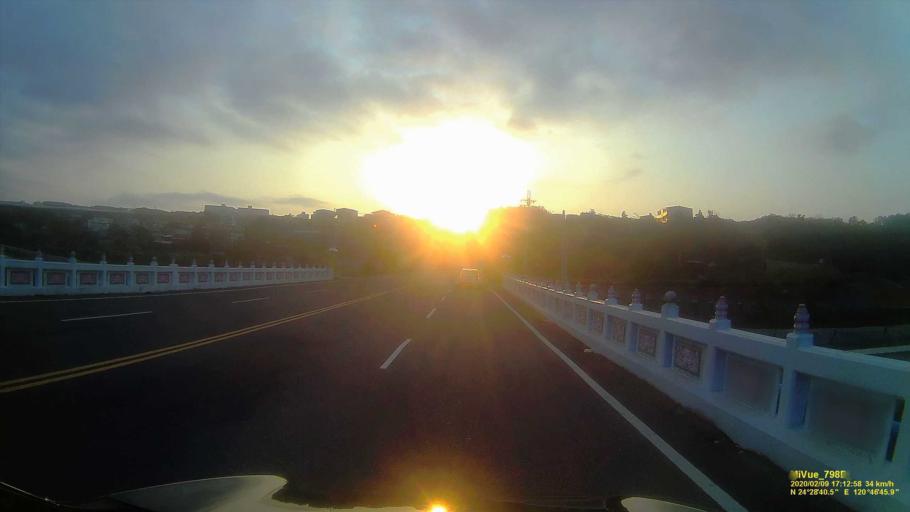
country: TW
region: Taiwan
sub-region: Miaoli
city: Miaoli
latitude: 24.4778
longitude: 120.7796
